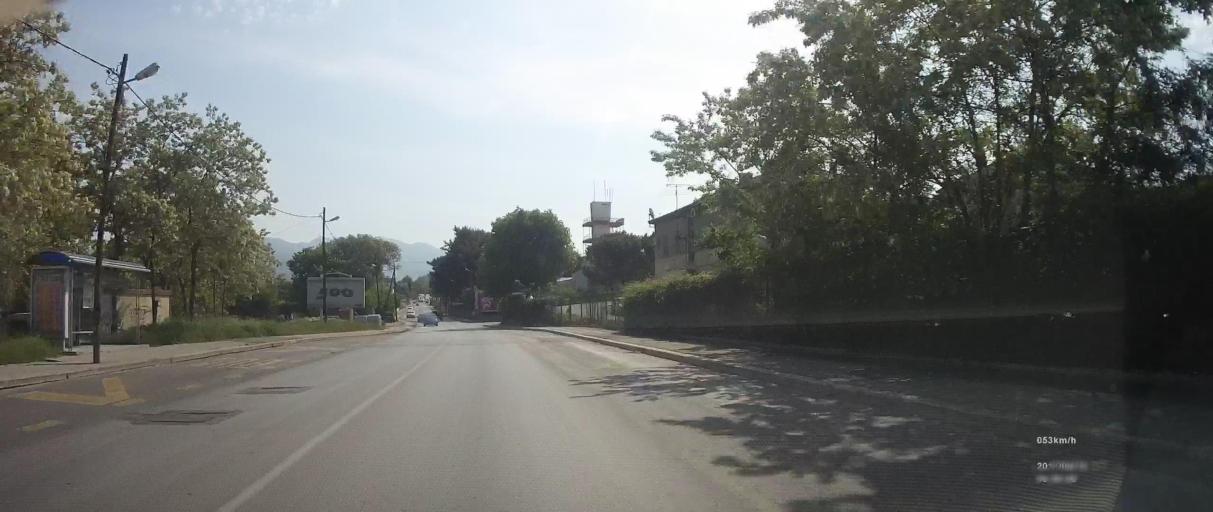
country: HR
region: Splitsko-Dalmatinska
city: Vranjic
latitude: 43.5213
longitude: 16.4563
